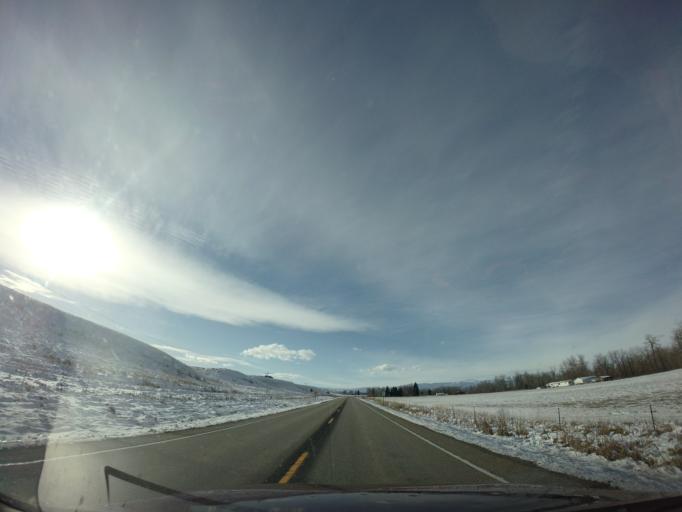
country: US
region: Montana
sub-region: Carbon County
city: Red Lodge
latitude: 45.3888
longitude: -109.1348
